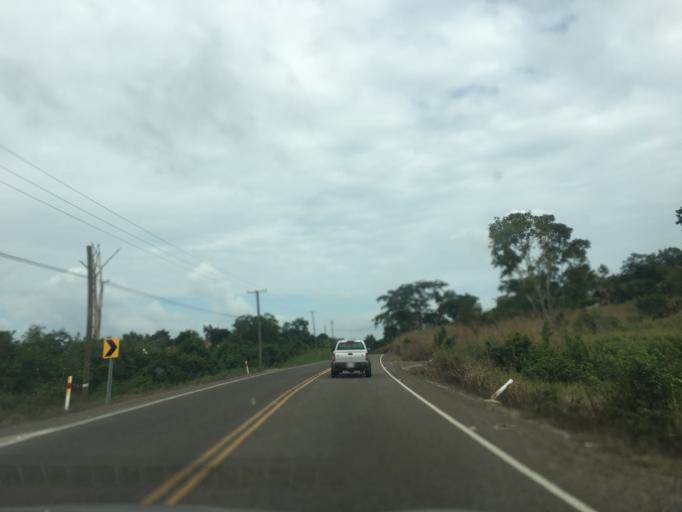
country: BZ
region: Cayo
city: Belmopan
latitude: 17.2275
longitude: -88.7795
